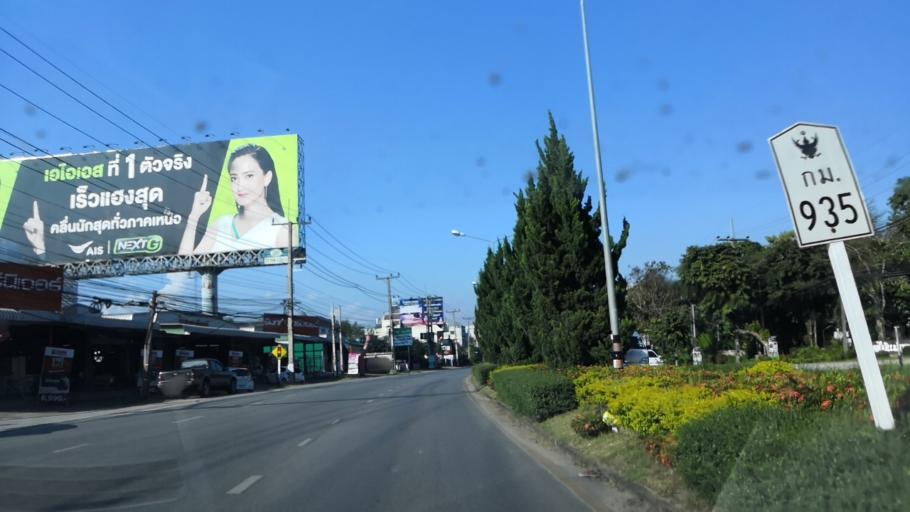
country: TH
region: Chiang Rai
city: Chiang Rai
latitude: 19.9265
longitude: 99.8442
